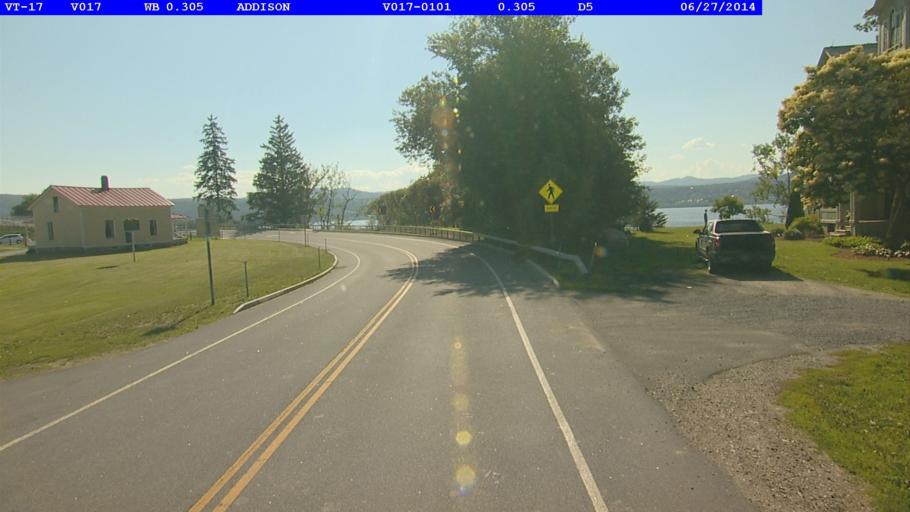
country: US
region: New York
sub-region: Essex County
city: Port Henry
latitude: 44.0362
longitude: -73.4197
